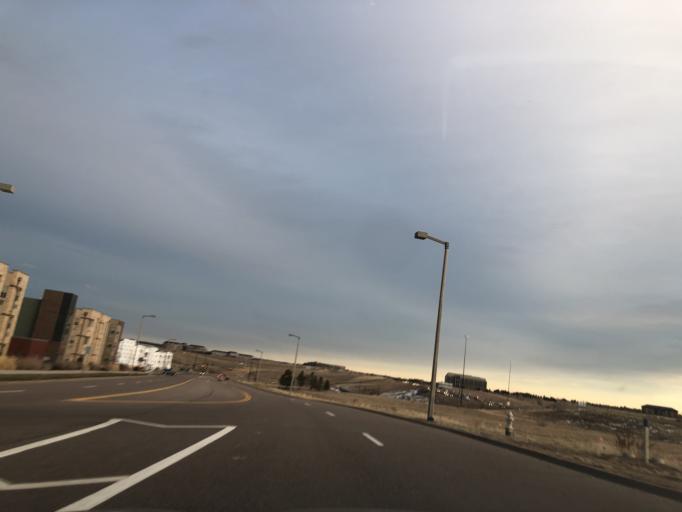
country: US
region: Colorado
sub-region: Douglas County
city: Meridian
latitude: 39.5571
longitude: -104.8675
